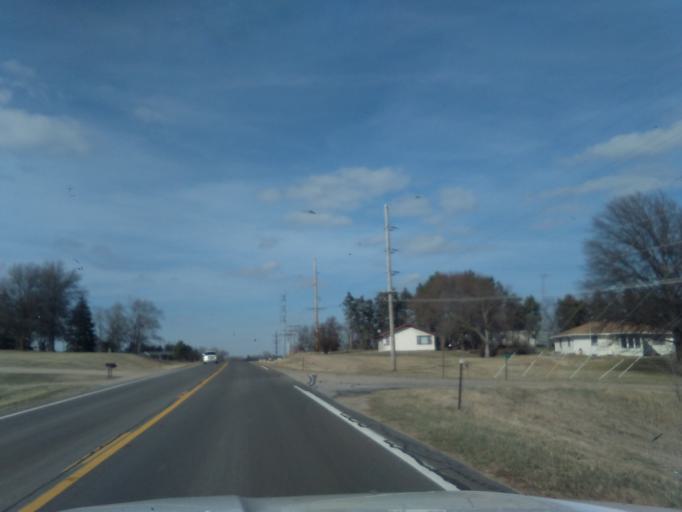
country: US
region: Nebraska
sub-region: Gage County
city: Beatrice
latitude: 40.1172
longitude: -96.9351
